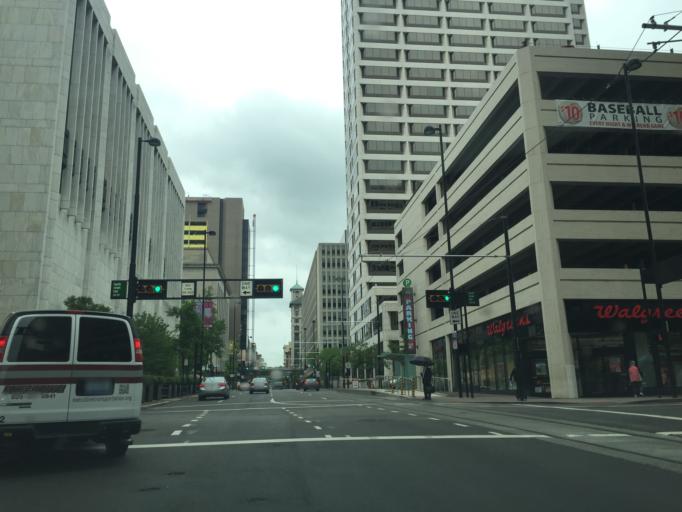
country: US
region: Kentucky
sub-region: Campbell County
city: Newport
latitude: 39.1003
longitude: -84.5095
